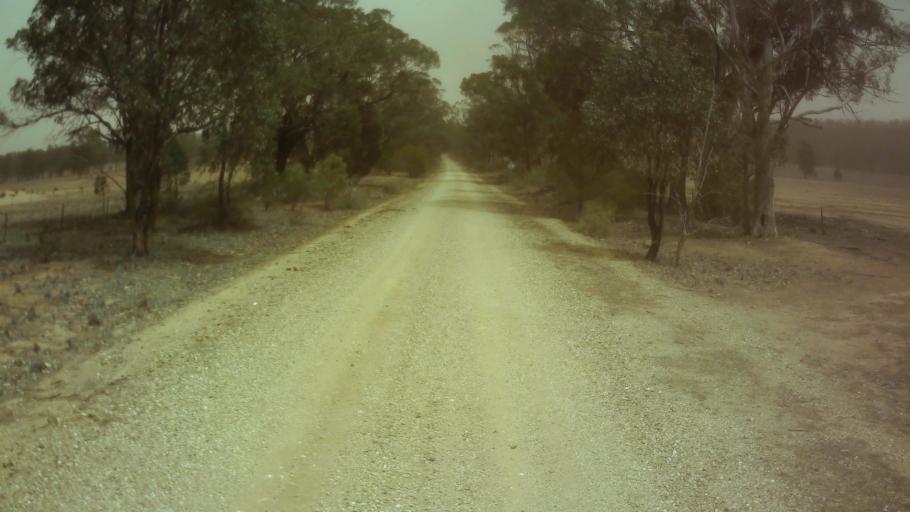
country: AU
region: New South Wales
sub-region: Weddin
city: Grenfell
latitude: -33.7105
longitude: 147.9567
